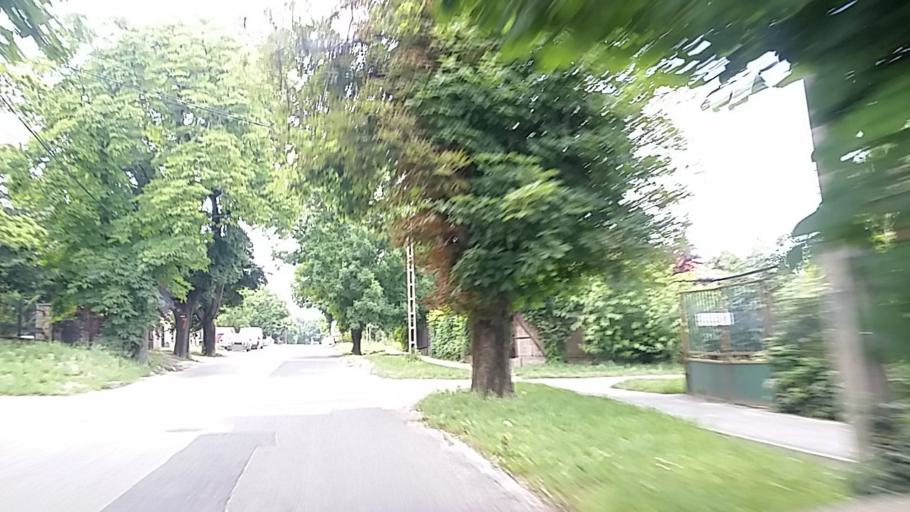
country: HU
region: Pest
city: Erd
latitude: 47.3850
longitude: 18.9381
